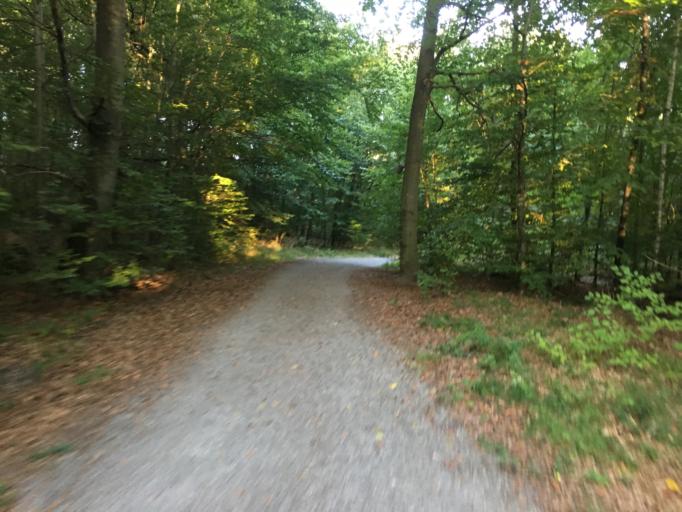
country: DE
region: Baden-Wuerttemberg
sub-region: Regierungsbezirk Stuttgart
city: Boeblingen
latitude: 48.6668
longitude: 8.9883
